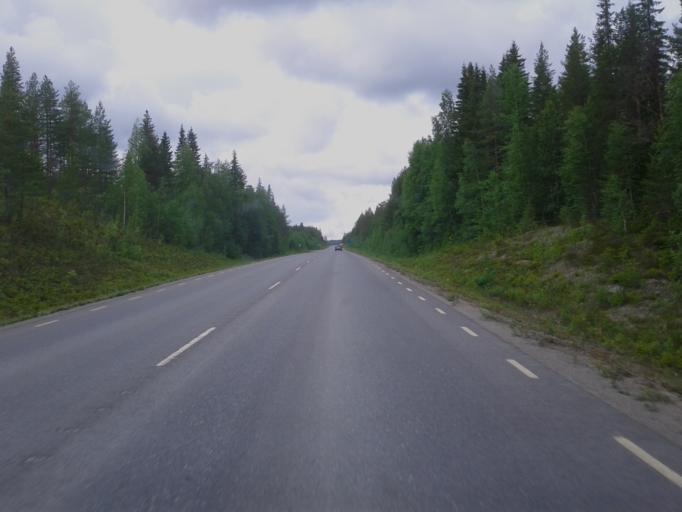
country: SE
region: Vaesterbotten
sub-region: Norsjo Kommun
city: Norsjoe
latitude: 64.9874
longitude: 19.4528
